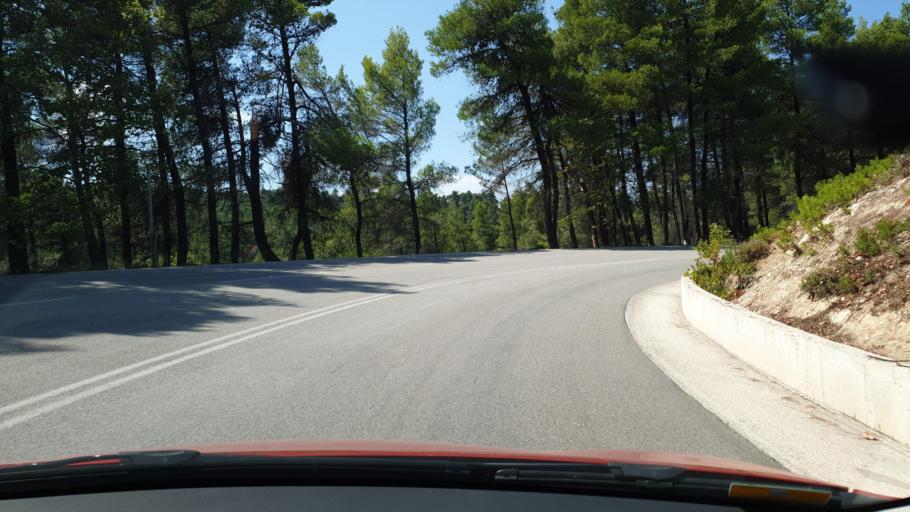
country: GR
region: Central Greece
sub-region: Nomos Evvoias
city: Politika
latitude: 38.6537
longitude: 23.5617
